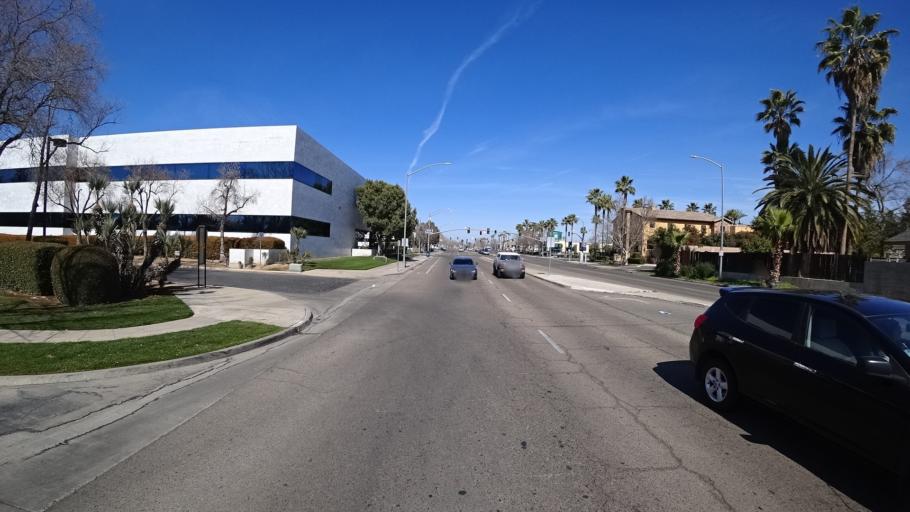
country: US
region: California
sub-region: Fresno County
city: Fresno
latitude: 36.8351
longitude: -119.8084
